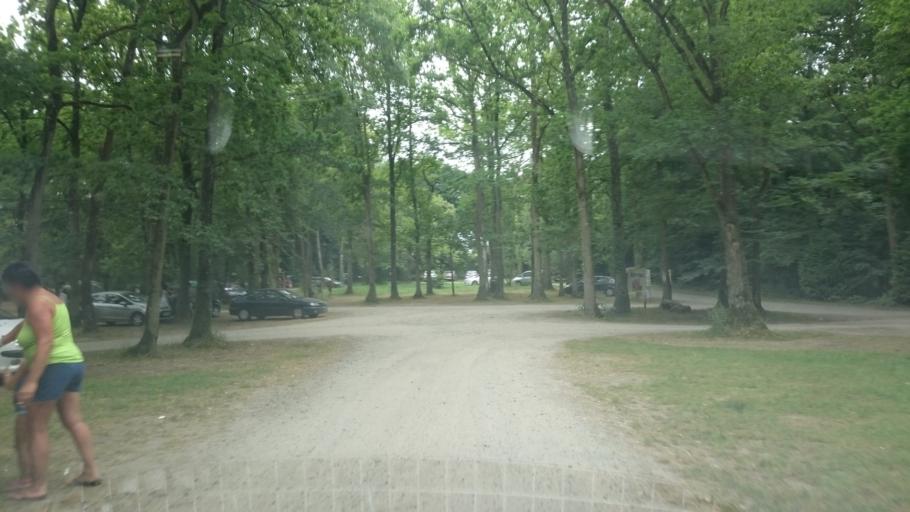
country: FR
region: Brittany
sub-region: Departement d'Ille-et-Vilaine
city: Meillac
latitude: 48.4379
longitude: -1.8330
